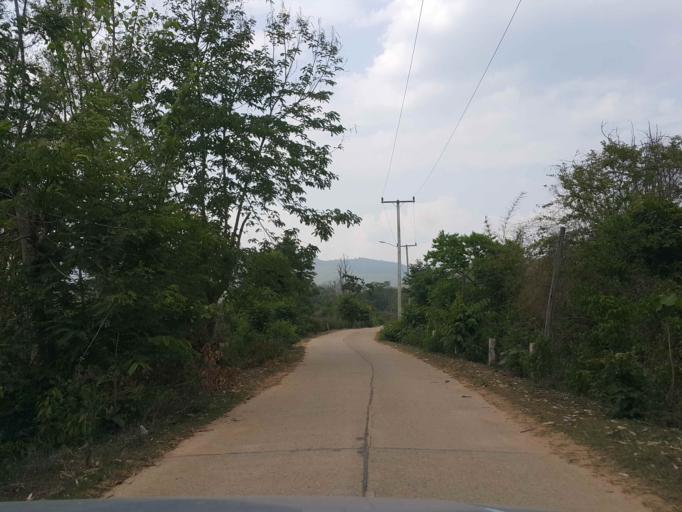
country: TH
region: Chiang Mai
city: Wiang Haeng
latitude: 19.4032
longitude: 98.7226
